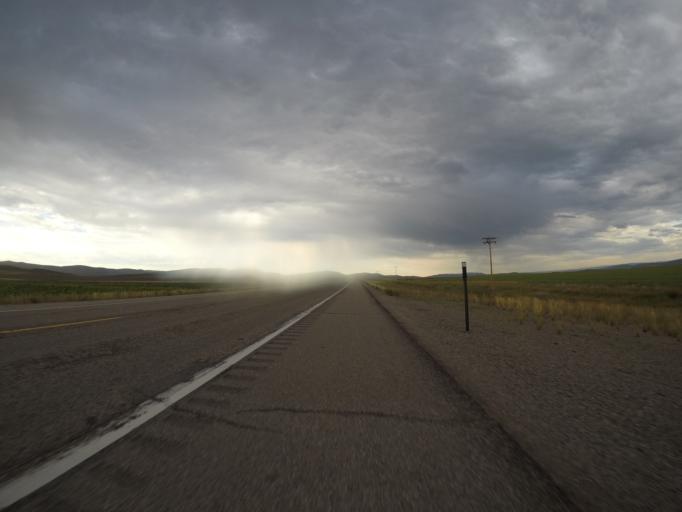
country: US
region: Utah
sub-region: Rich County
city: Randolph
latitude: 41.9219
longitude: -110.9549
